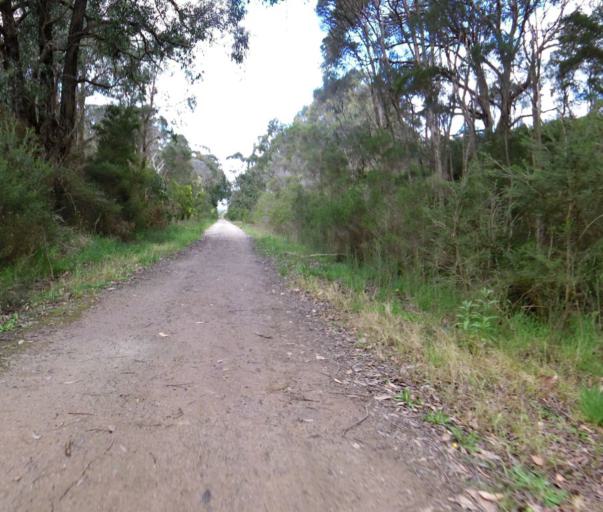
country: AU
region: Victoria
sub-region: Bass Coast
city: North Wonthaggi
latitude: -38.6829
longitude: 146.0528
